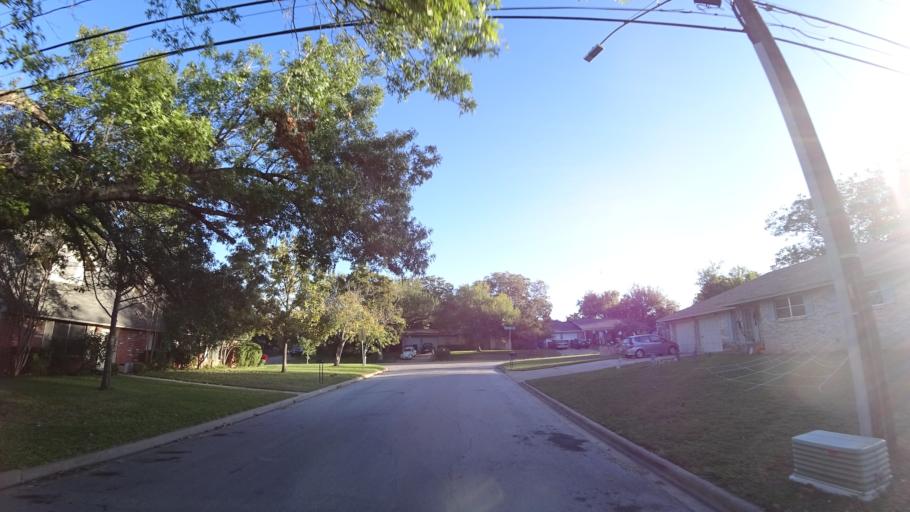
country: US
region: Texas
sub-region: Travis County
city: Austin
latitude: 30.3019
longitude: -97.6791
